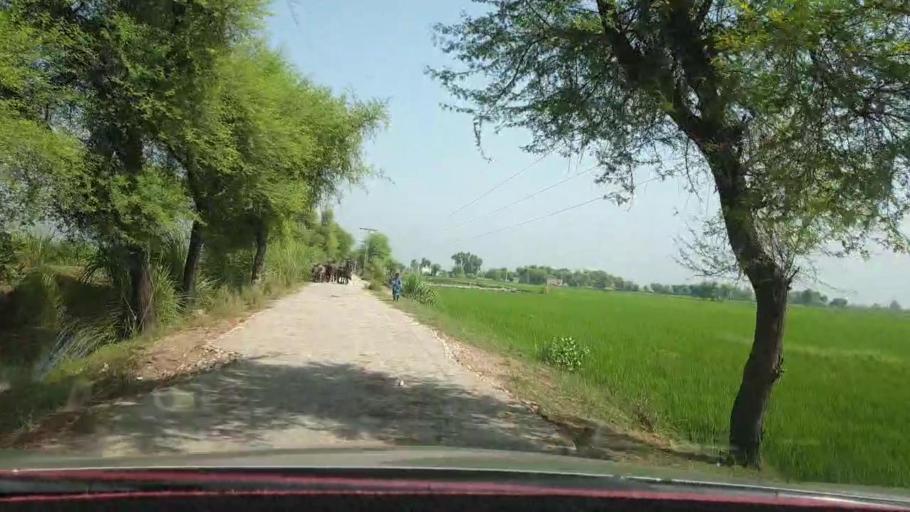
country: PK
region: Sindh
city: Warah
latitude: 27.4941
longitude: 67.8356
